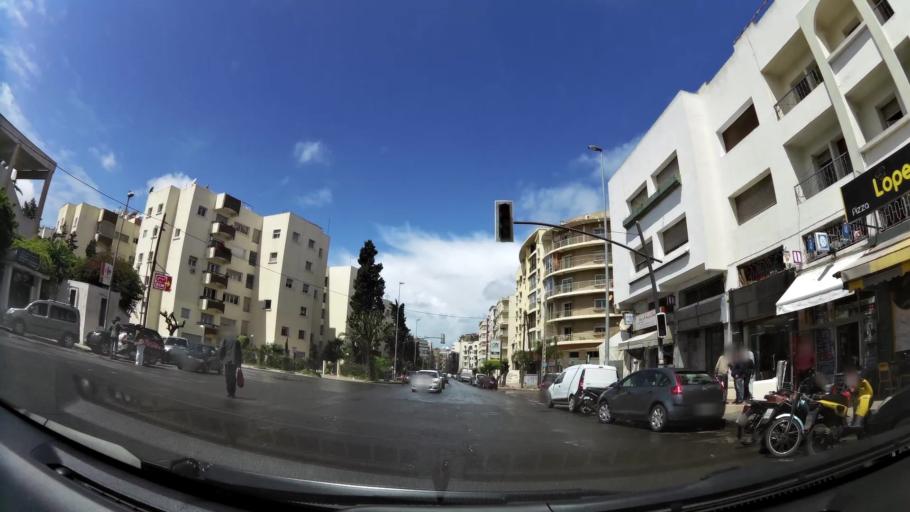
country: MA
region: Grand Casablanca
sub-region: Casablanca
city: Casablanca
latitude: 33.5728
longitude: -7.6387
